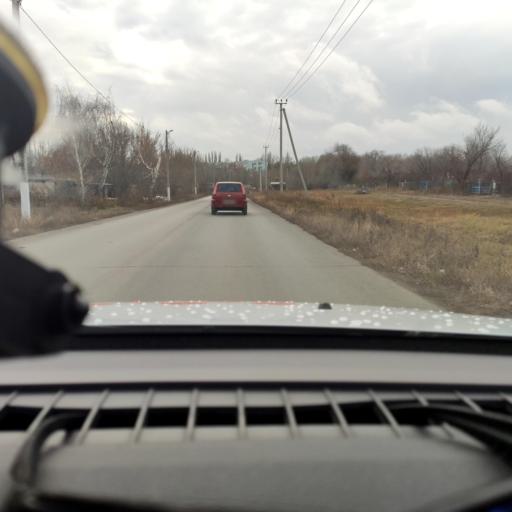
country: RU
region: Samara
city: Chapayevsk
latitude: 52.9891
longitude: 49.7263
